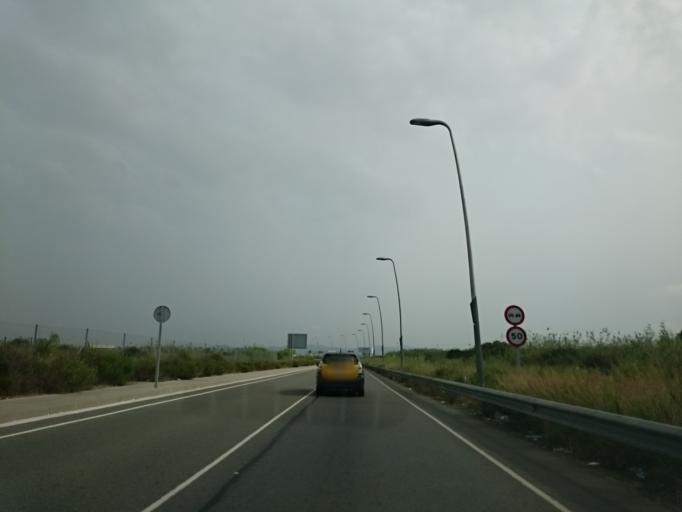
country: ES
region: Catalonia
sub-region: Provincia de Barcelona
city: Viladecans
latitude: 41.2883
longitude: 2.0548
